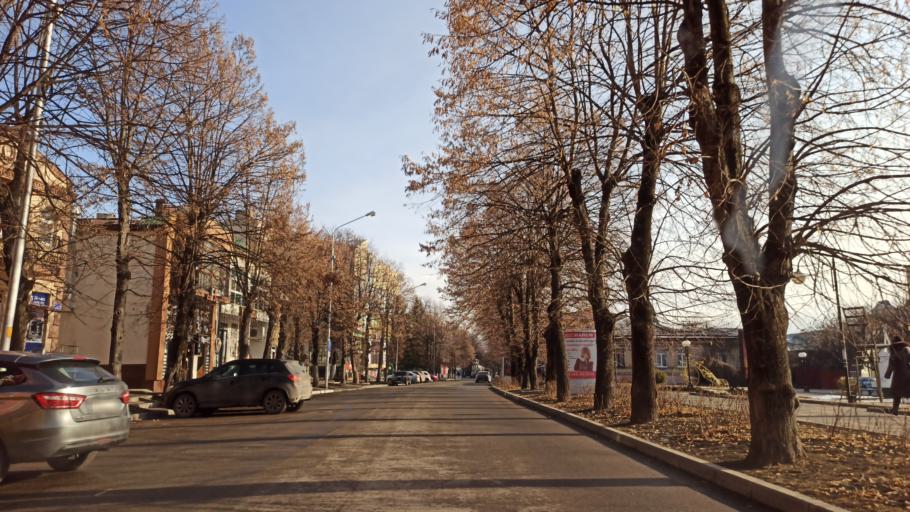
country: RU
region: Stavropol'skiy
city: Yessentuki
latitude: 44.0433
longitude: 42.8564
